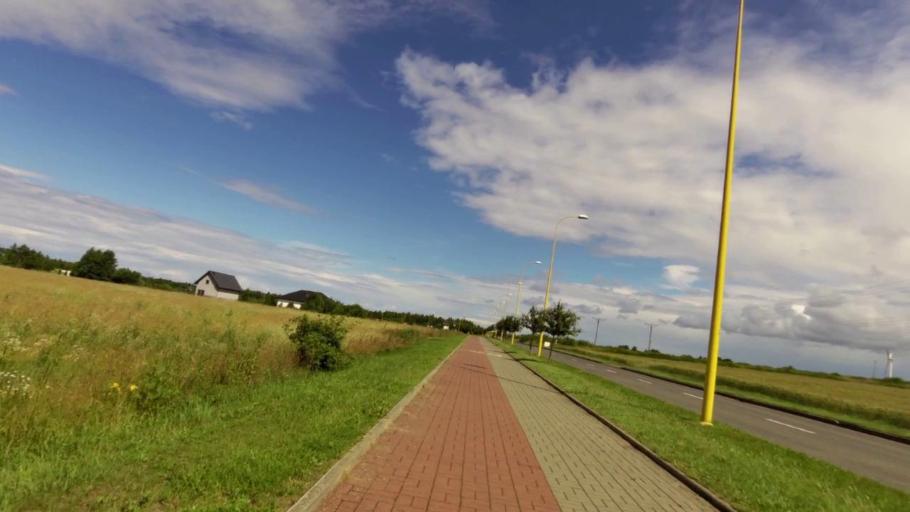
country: PL
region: West Pomeranian Voivodeship
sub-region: Powiat slawienski
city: Darlowo
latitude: 54.4396
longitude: 16.4076
